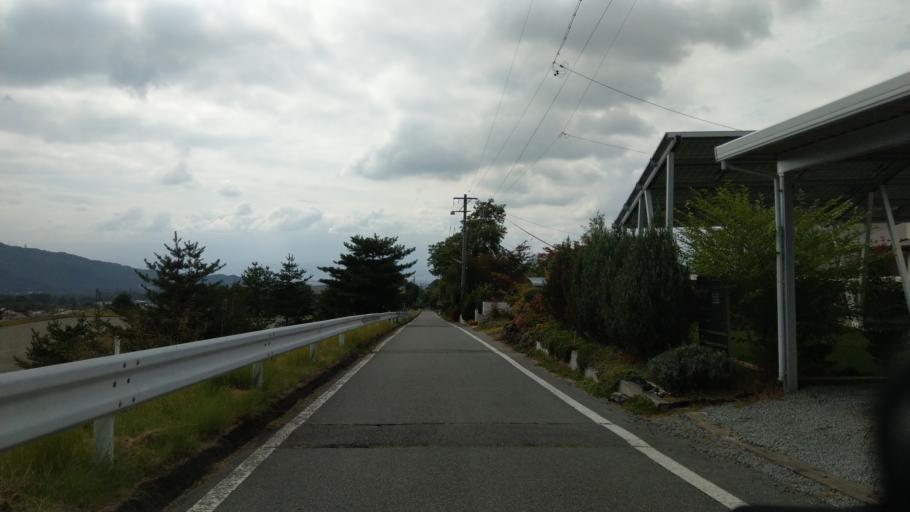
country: JP
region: Nagano
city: Komoro
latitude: 36.3239
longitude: 138.5274
